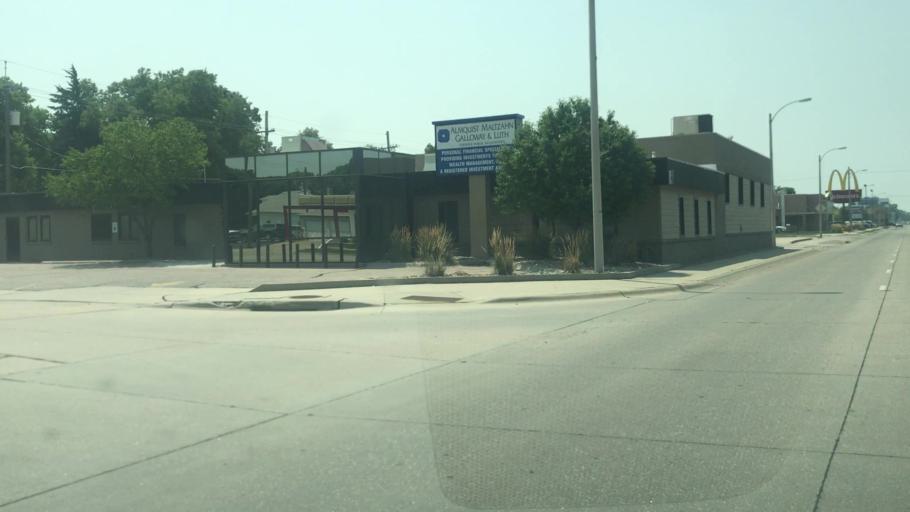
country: US
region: Nebraska
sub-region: Hall County
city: Grand Island
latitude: 40.9201
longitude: -98.3514
